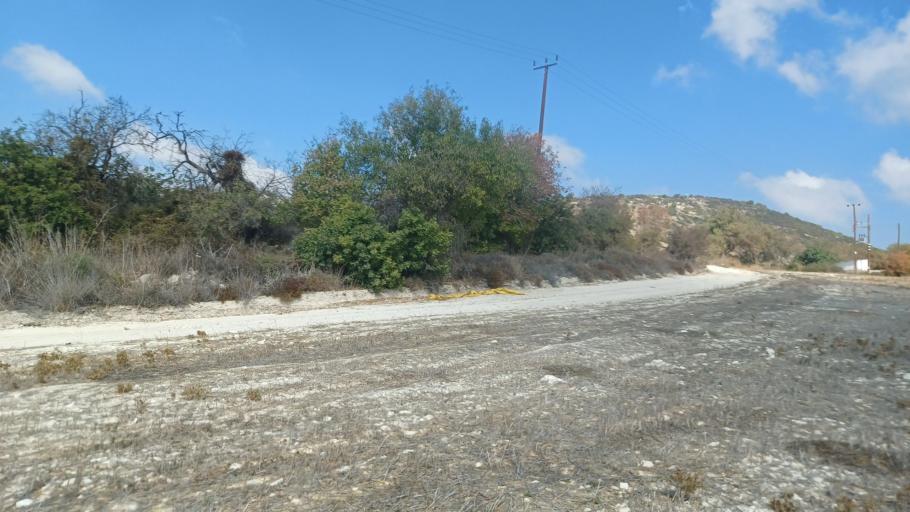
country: CY
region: Pafos
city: Mesogi
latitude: 34.8332
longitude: 32.4567
